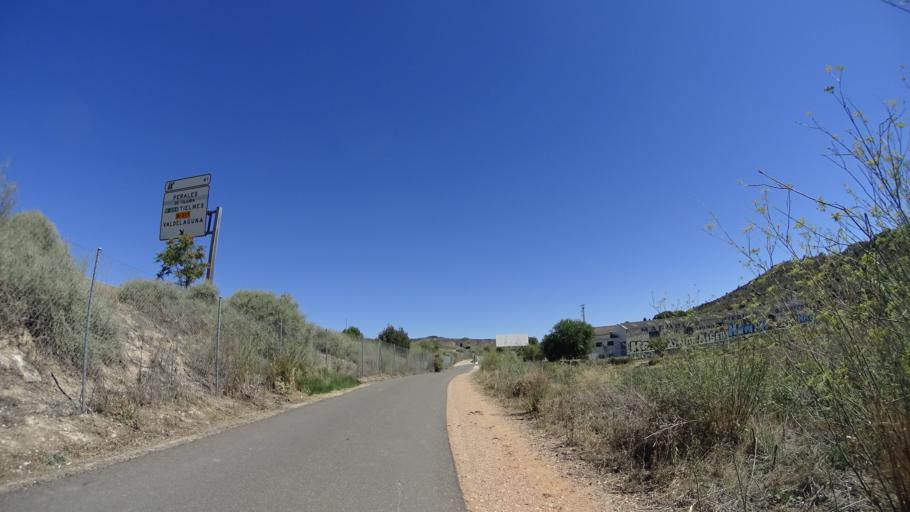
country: ES
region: Madrid
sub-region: Provincia de Madrid
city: Perales de Tajuna
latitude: 40.2270
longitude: -3.3367
